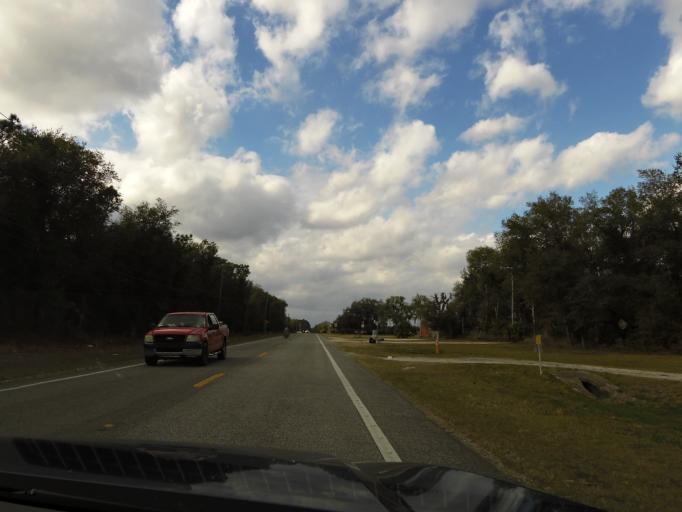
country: US
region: Florida
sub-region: Volusia County
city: Pierson
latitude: 29.2044
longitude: -81.4427
